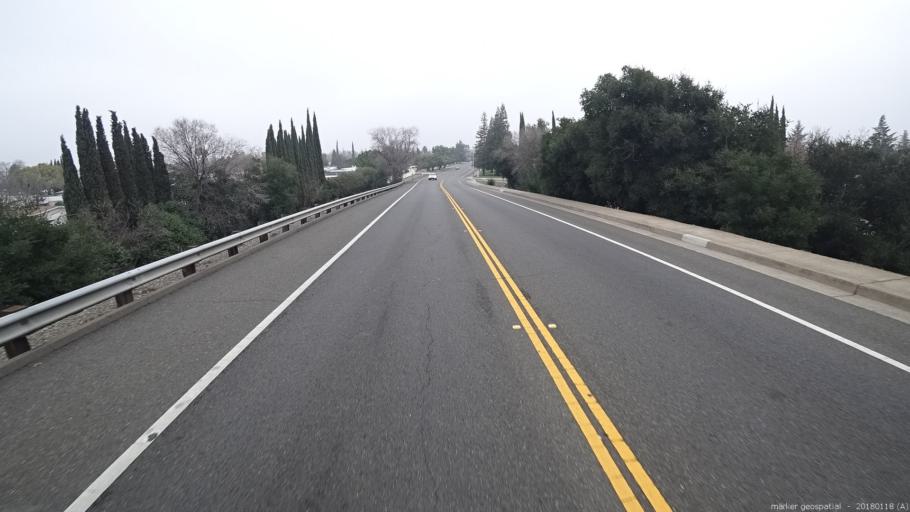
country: US
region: California
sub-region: Sacramento County
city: Rancho Cordova
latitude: 38.5758
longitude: -121.3181
